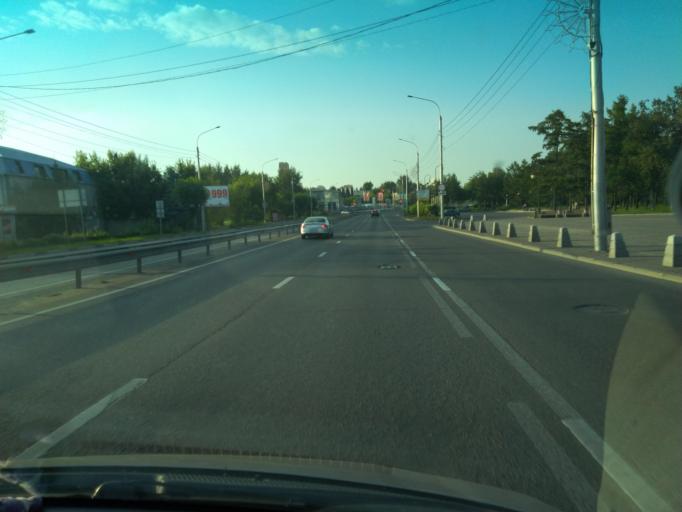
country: RU
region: Krasnoyarskiy
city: Krasnoyarsk
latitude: 56.0220
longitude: 92.8853
